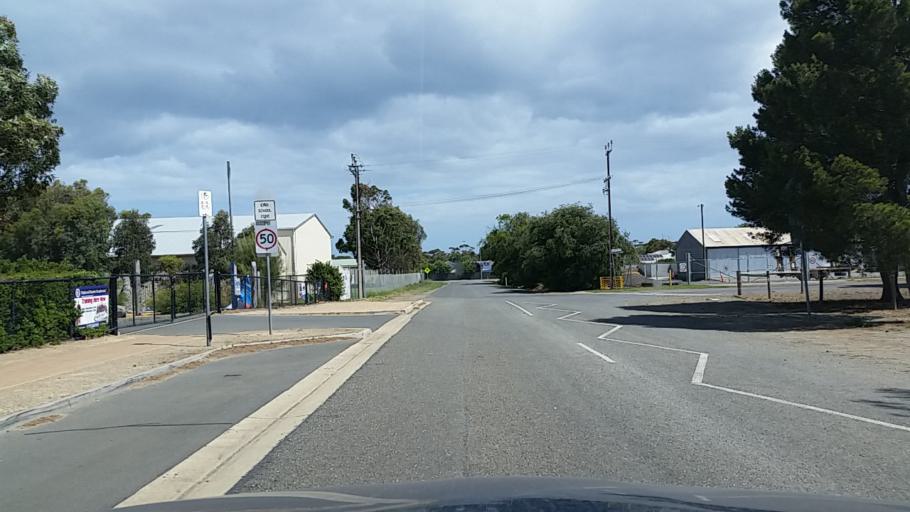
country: AU
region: South Australia
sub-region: Alexandrina
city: Port Elliot
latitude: -35.5239
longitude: 138.6770
